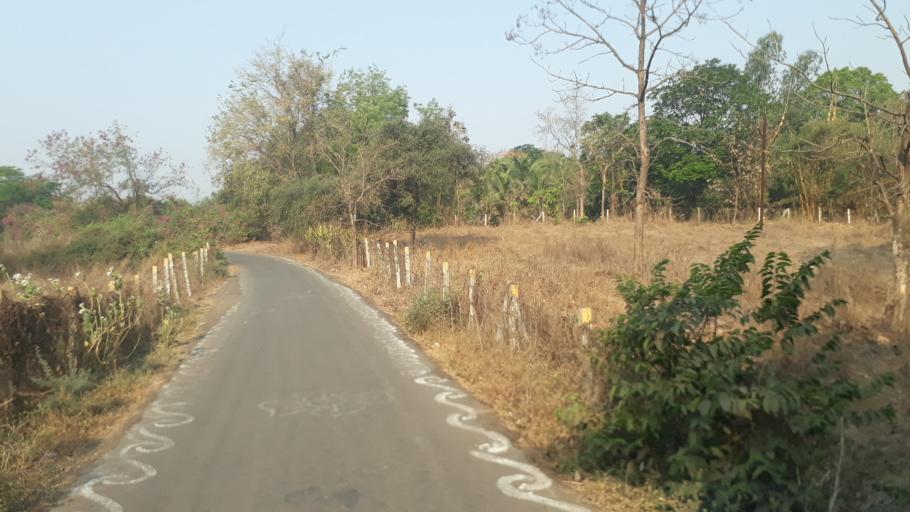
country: IN
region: Maharashtra
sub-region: Raigarh
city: Neral
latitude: 19.0477
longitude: 73.3325
